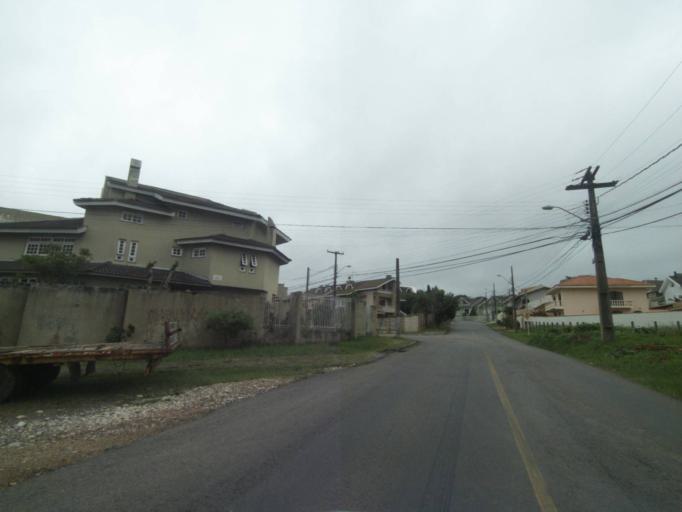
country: BR
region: Parana
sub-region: Curitiba
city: Curitiba
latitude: -25.4248
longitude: -49.3464
